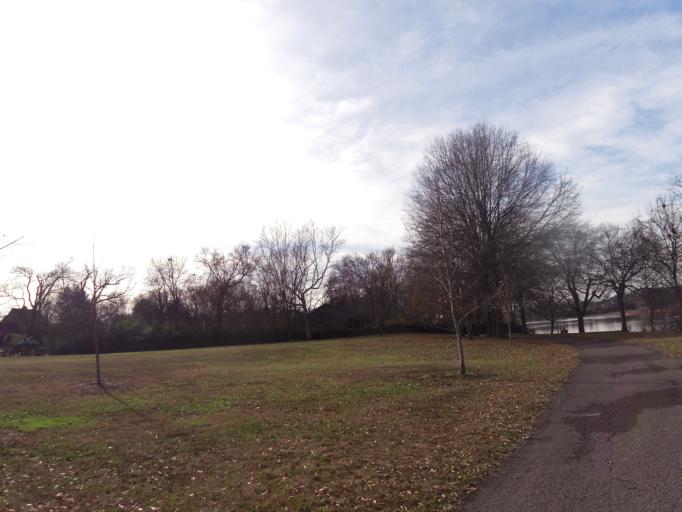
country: US
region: Tennessee
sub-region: Knox County
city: Knoxville
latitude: 35.9616
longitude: -83.8836
